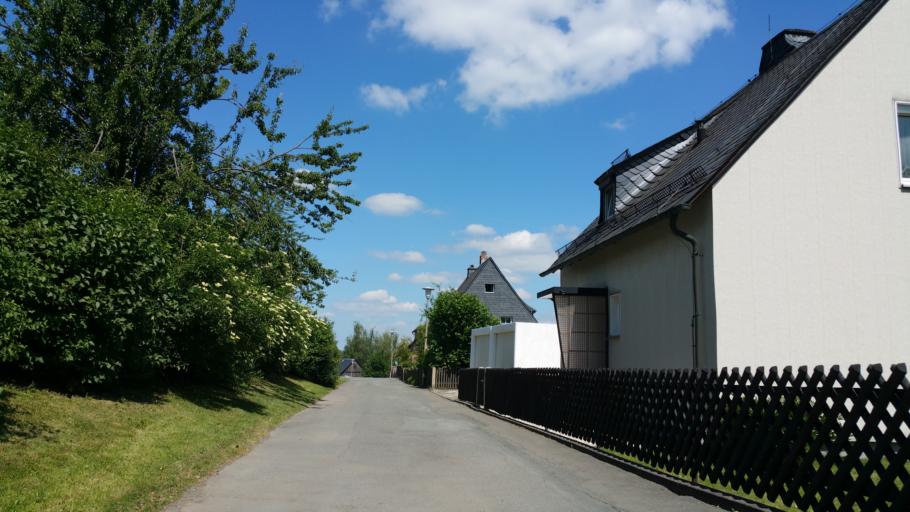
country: DE
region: Bavaria
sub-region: Upper Franconia
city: Schwarzenbach an der Saale
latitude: 50.2193
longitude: 11.9278
